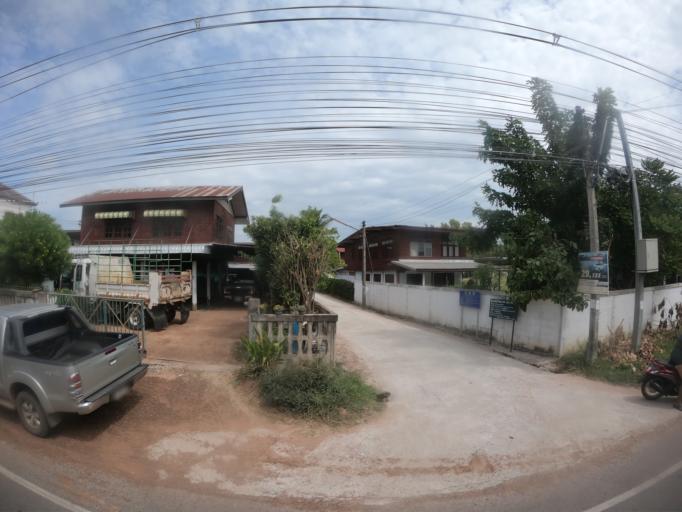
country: TH
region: Maha Sarakham
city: Chiang Yuen
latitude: 16.3477
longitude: 103.1221
